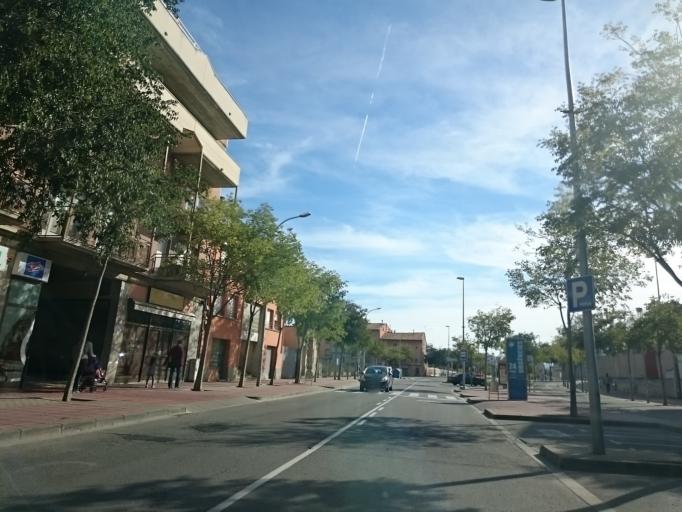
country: ES
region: Catalonia
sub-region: Provincia de Barcelona
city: Vic
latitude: 41.9300
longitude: 2.2612
